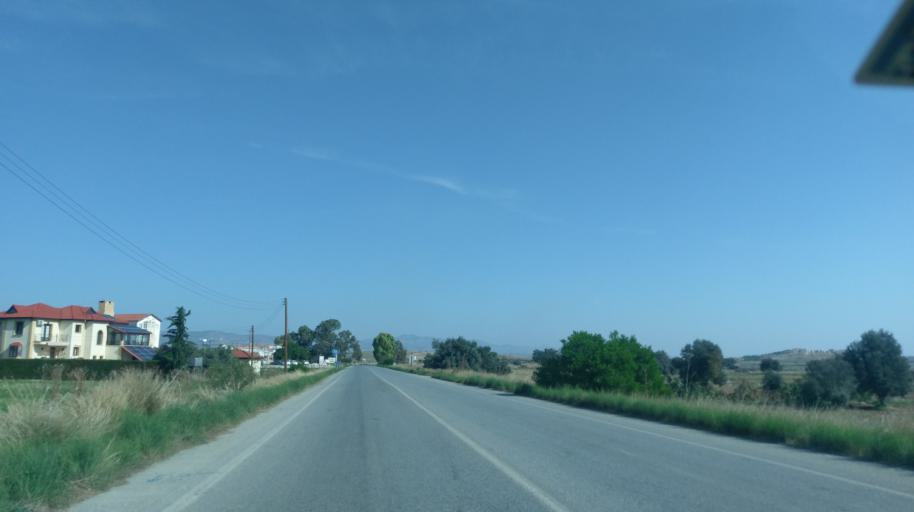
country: CY
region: Ammochostos
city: Lefkonoiko
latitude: 35.2449
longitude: 33.6081
